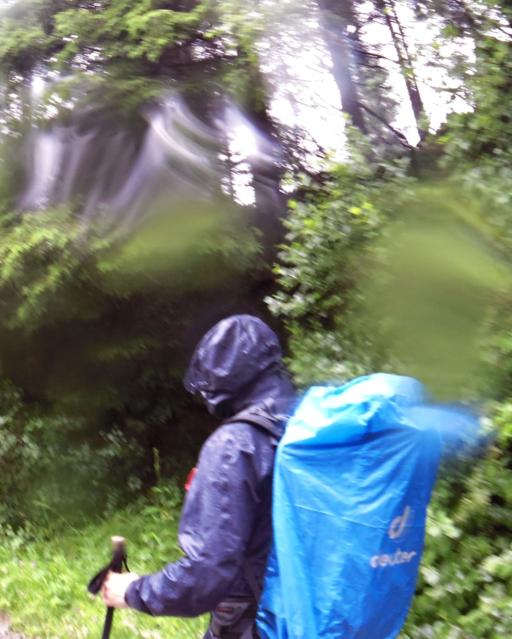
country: AT
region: Tyrol
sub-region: Politischer Bezirk Innsbruck Land
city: Neustift im Stubaital
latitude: 47.0209
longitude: 11.2227
